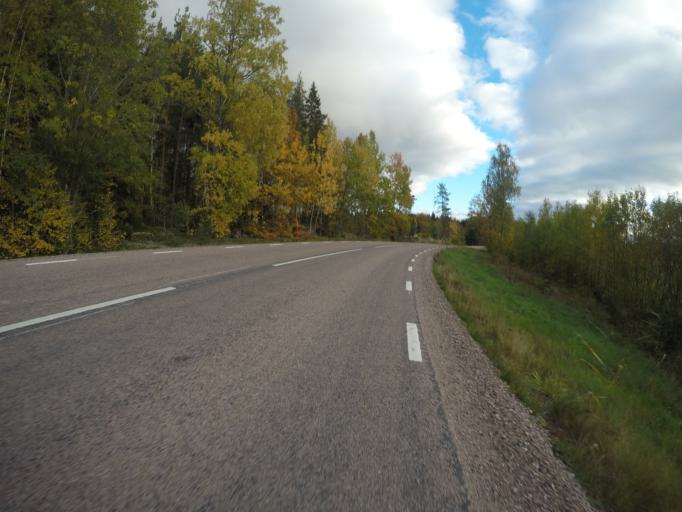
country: SE
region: Vaestmanland
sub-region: Arboga Kommun
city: Tyringe
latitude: 59.3133
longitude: 15.9853
